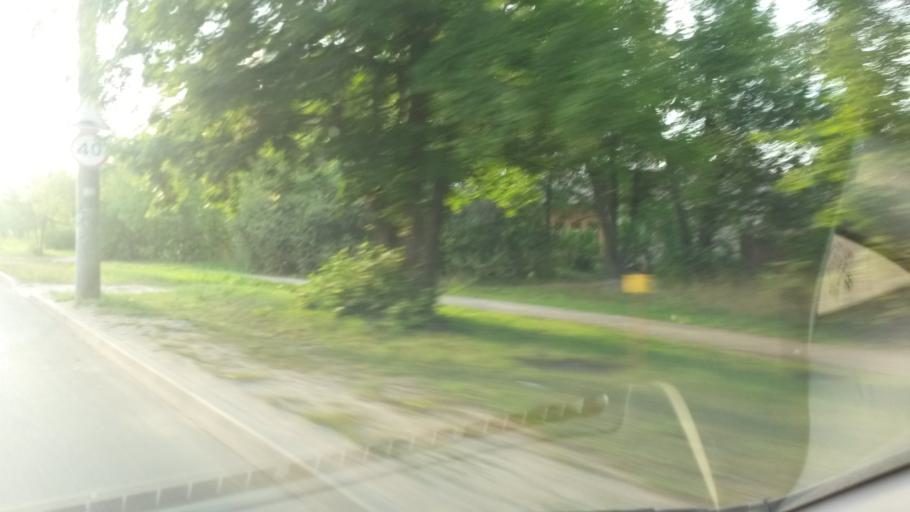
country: RU
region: Ivanovo
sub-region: Gorod Ivanovo
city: Ivanovo
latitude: 57.0102
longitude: 40.9414
